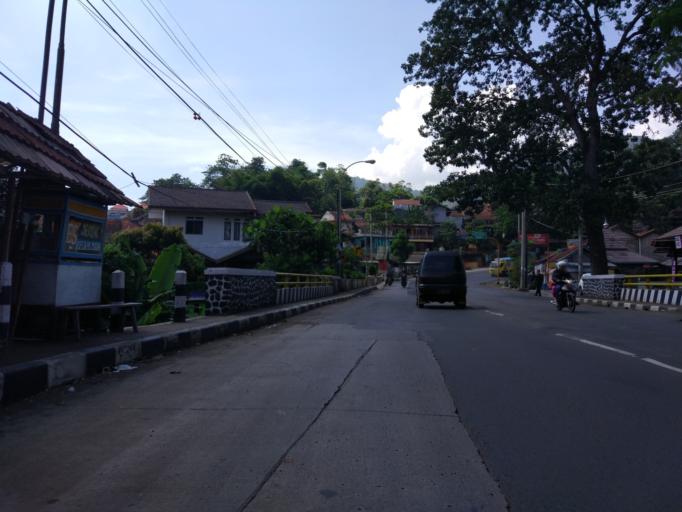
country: ID
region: West Java
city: Cileunyi
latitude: -6.9285
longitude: 107.7818
